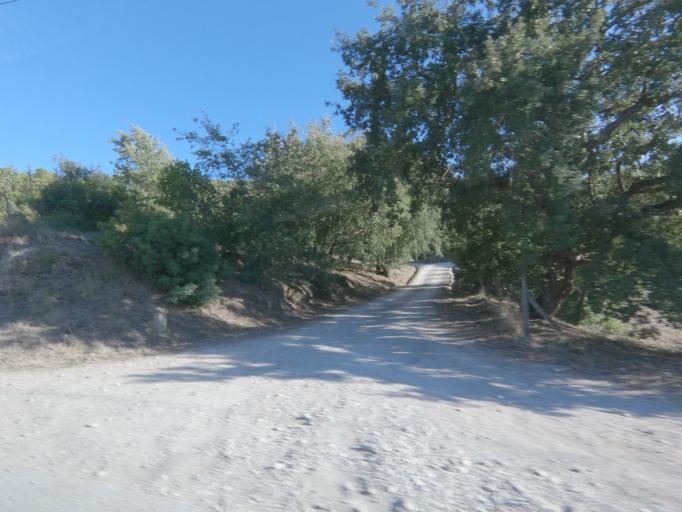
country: PT
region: Setubal
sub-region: Palmela
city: Quinta do Anjo
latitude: 38.5040
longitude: -8.9673
